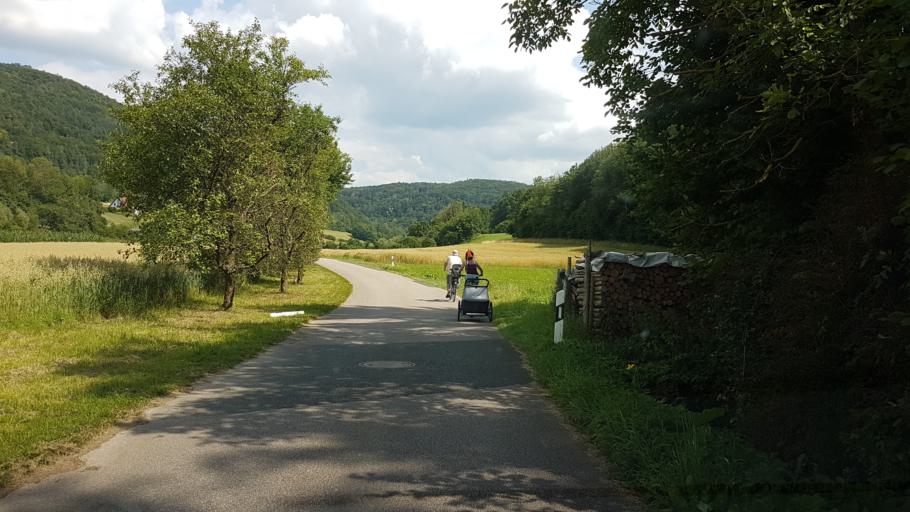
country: DE
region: Bavaria
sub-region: Upper Franconia
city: Egloffstein
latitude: 49.7282
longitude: 11.2415
